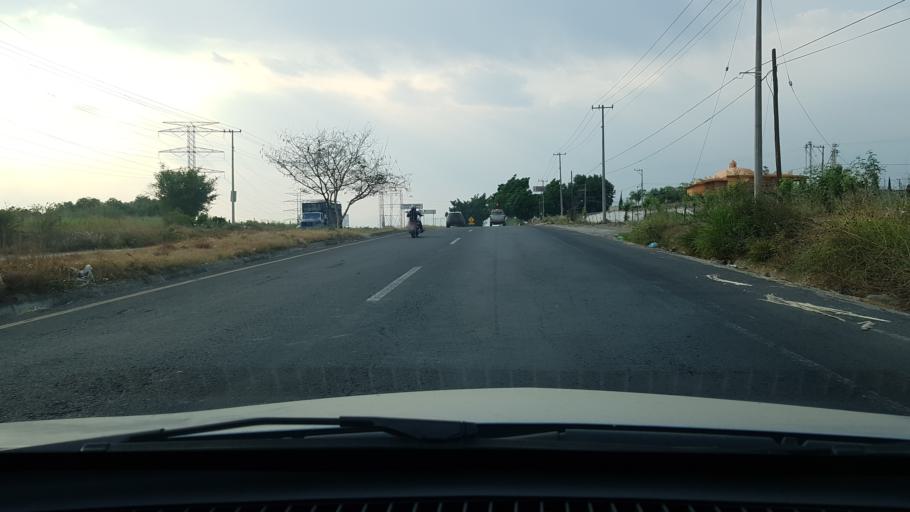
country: MX
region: Morelos
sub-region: Cuautla
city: Tierra Larga (Campo Nuevo)
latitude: 18.8425
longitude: -98.9272
